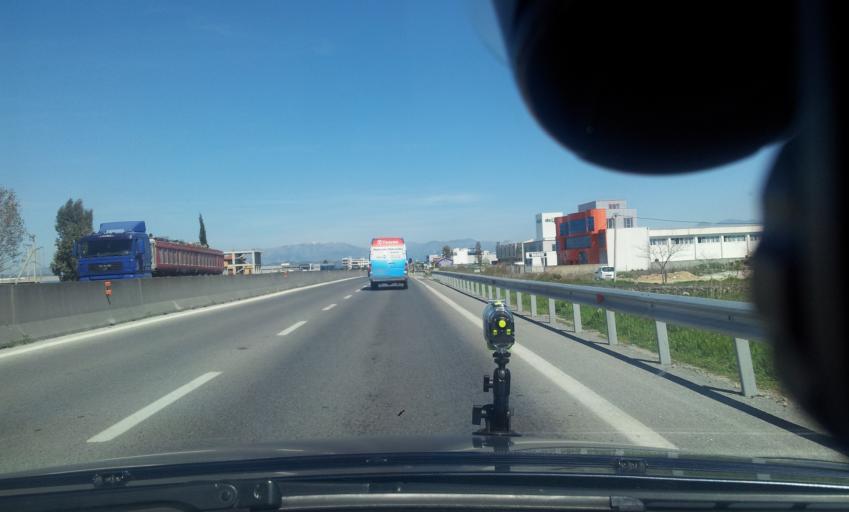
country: AL
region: Durres
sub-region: Rrethi i Durresit
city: Rrashbull
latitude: 41.3435
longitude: 19.4987
